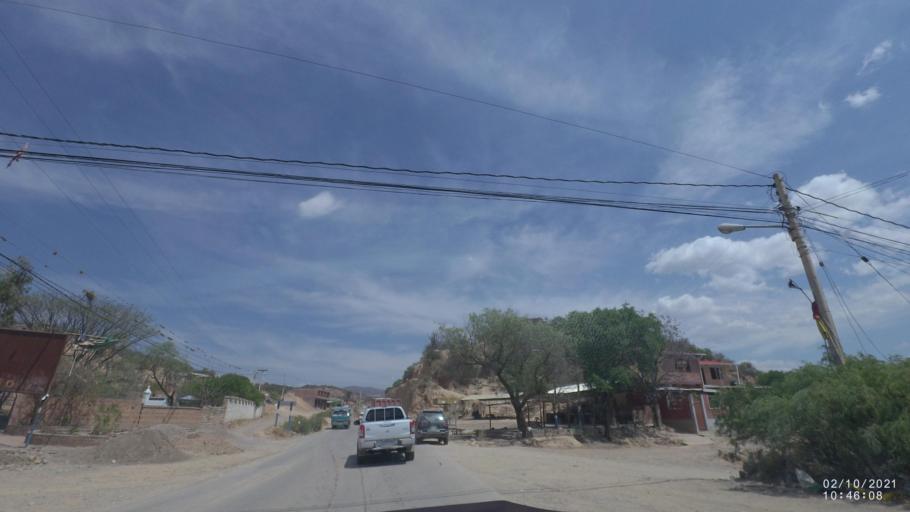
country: BO
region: Cochabamba
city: Capinota
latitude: -17.5860
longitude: -66.3218
